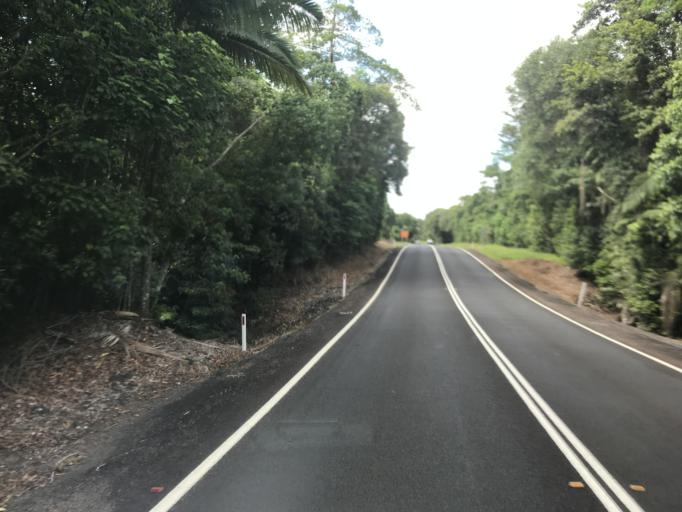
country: AU
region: Queensland
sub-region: Cassowary Coast
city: Innisfail
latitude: -17.8572
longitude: 146.0655
